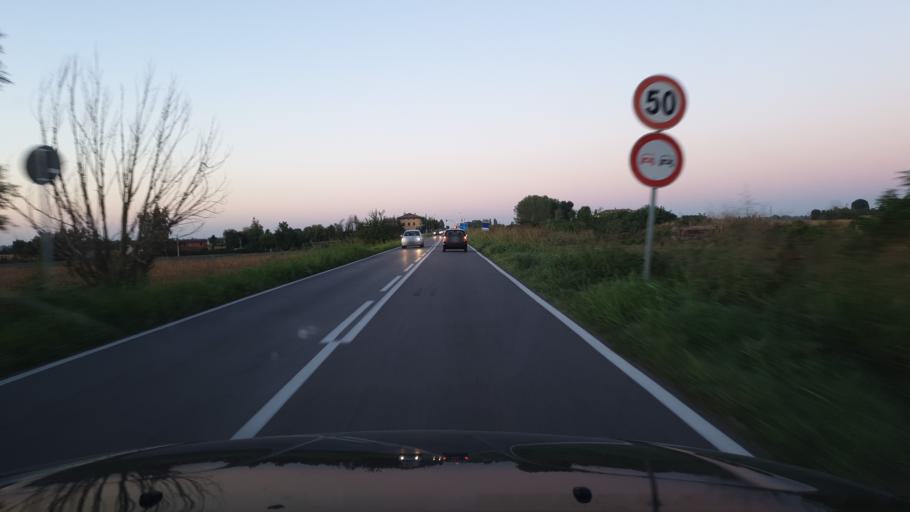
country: IT
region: Emilia-Romagna
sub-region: Provincia di Bologna
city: Minerbio
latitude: 44.6365
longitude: 11.4697
